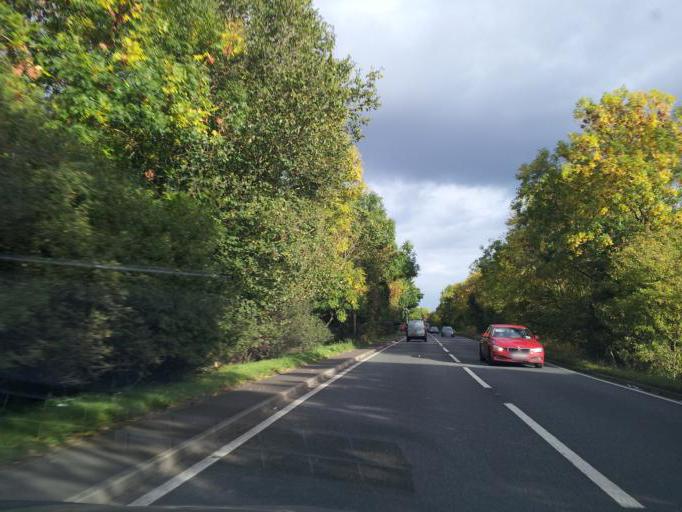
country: GB
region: England
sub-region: Cambridgeshire
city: Papworth Everard
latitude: 52.2222
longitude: -0.1538
